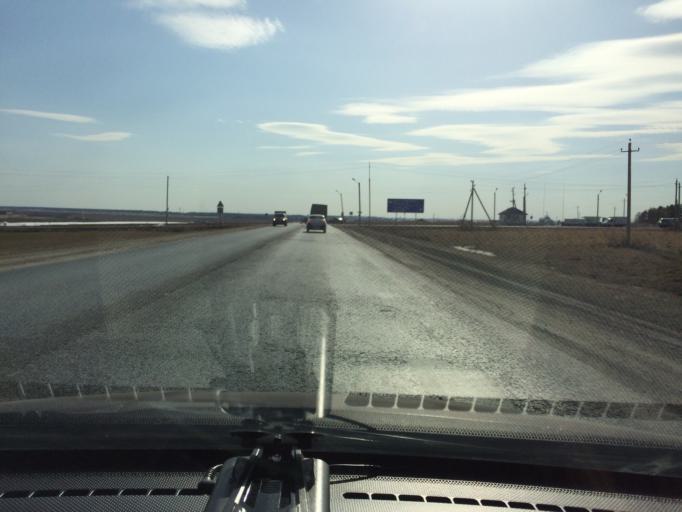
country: RU
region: Mariy-El
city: Yoshkar-Ola
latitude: 56.6975
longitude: 48.0622
